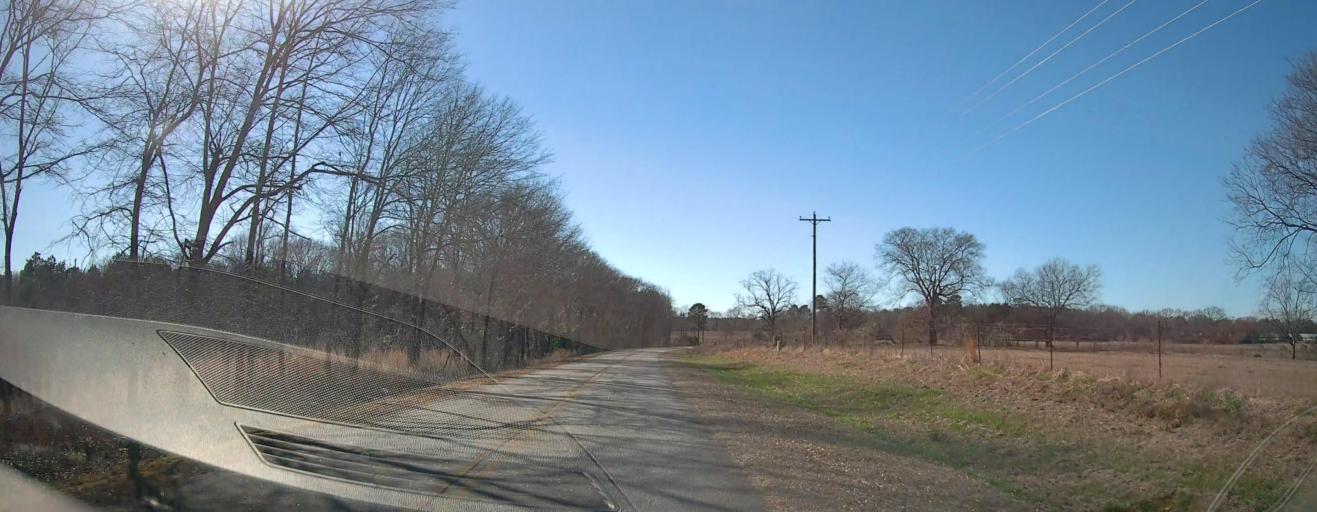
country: US
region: Georgia
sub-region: Taylor County
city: Butler
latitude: 32.6253
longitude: -84.2566
